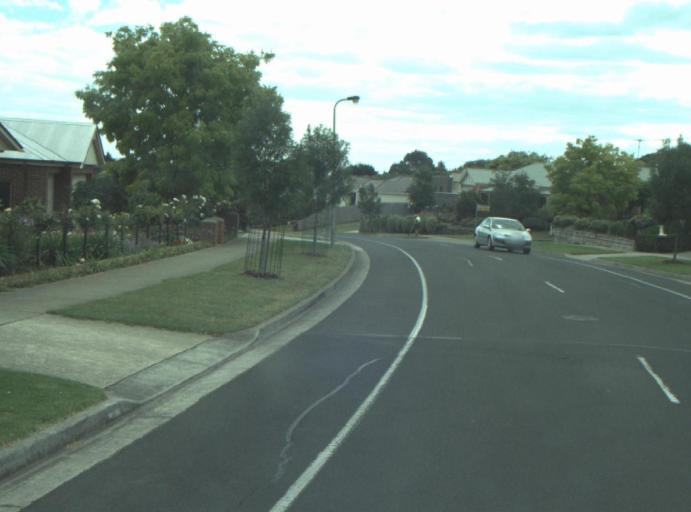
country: AU
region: Victoria
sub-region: Greater Geelong
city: Wandana Heights
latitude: -38.2049
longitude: 144.3140
